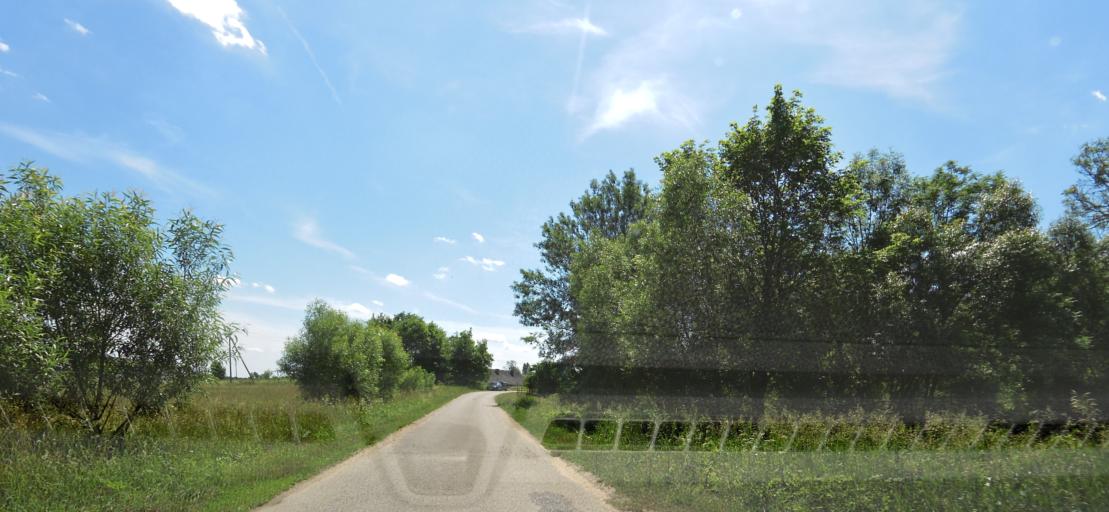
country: LT
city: Nemencine
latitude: 54.8995
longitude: 25.4822
